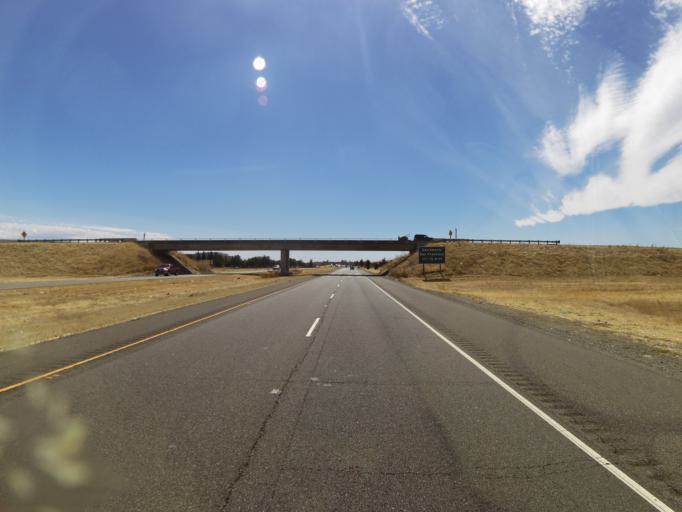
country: US
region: California
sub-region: Solano County
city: Hartley
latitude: 38.3951
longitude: -121.9497
